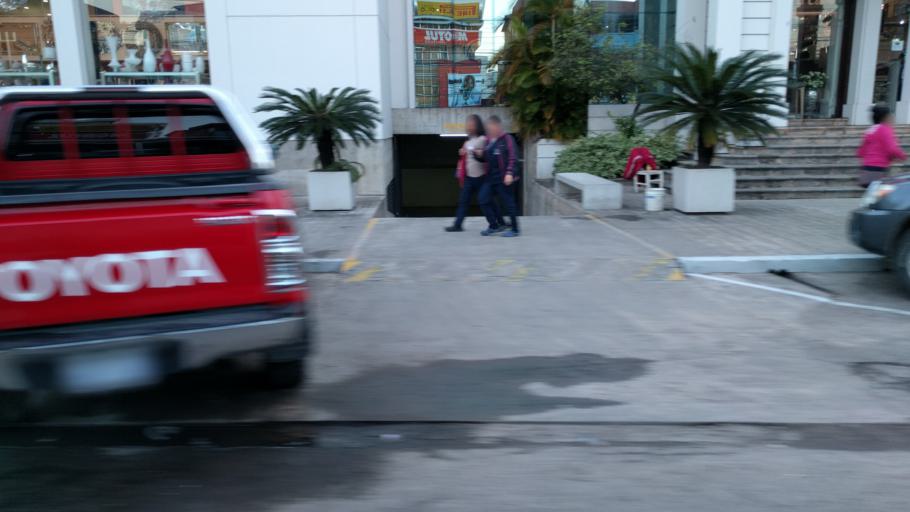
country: BO
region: Santa Cruz
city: Santa Cruz de la Sierra
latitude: -17.7816
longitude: -63.1891
